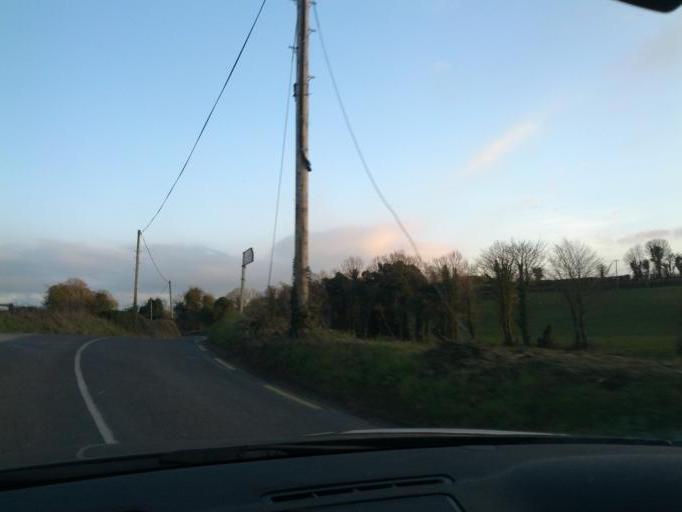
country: IE
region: Munster
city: Nenagh Bridge
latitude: 52.9561
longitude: -8.2340
